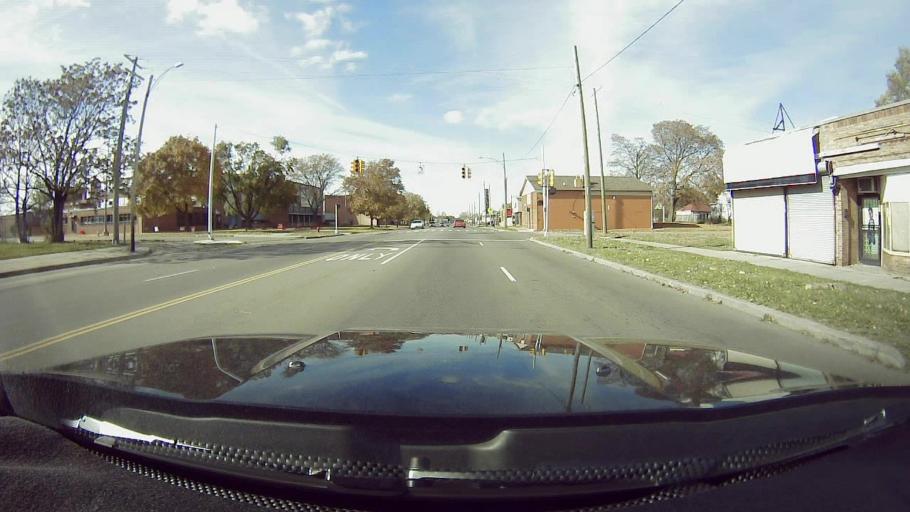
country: US
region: Michigan
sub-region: Macomb County
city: Warren
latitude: 42.4345
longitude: -83.0017
